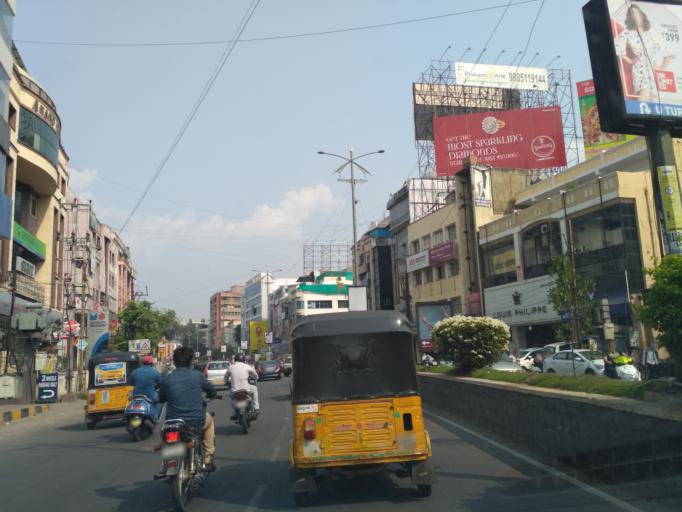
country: IN
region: Telangana
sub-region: Hyderabad
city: Hyderabad
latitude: 17.4023
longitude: 78.4837
